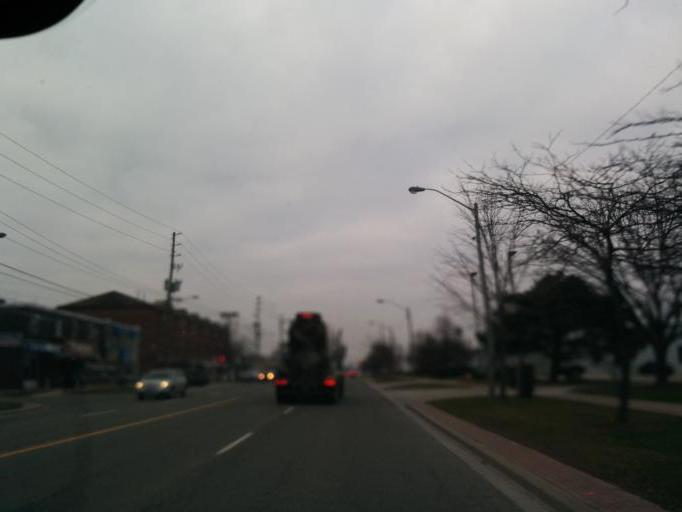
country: CA
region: Ontario
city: Etobicoke
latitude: 43.5998
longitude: -79.5443
